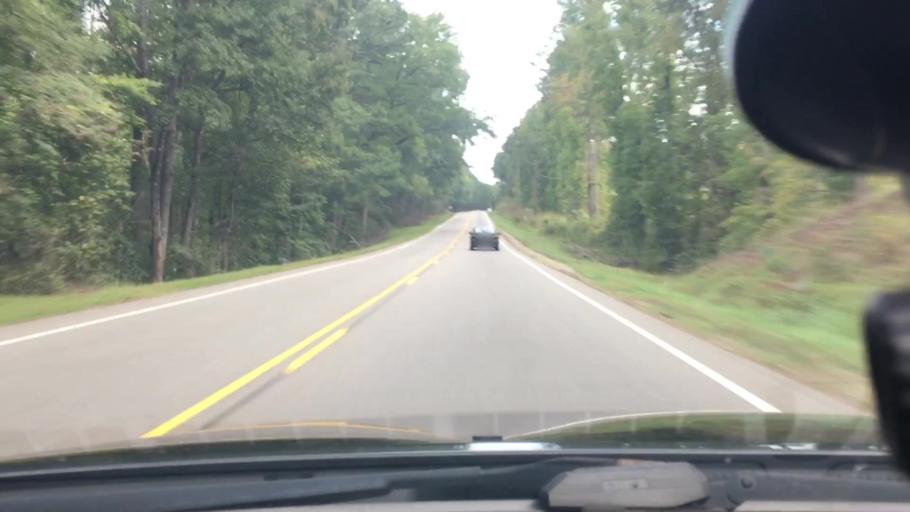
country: US
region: North Carolina
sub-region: Moore County
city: Carthage
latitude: 35.3612
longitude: -79.4395
